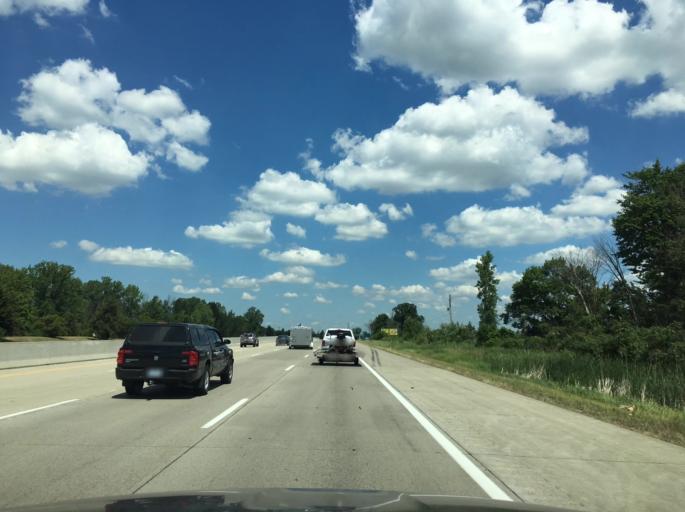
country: US
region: Michigan
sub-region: Saginaw County
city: Zilwaukee
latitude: 43.5286
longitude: -83.9422
